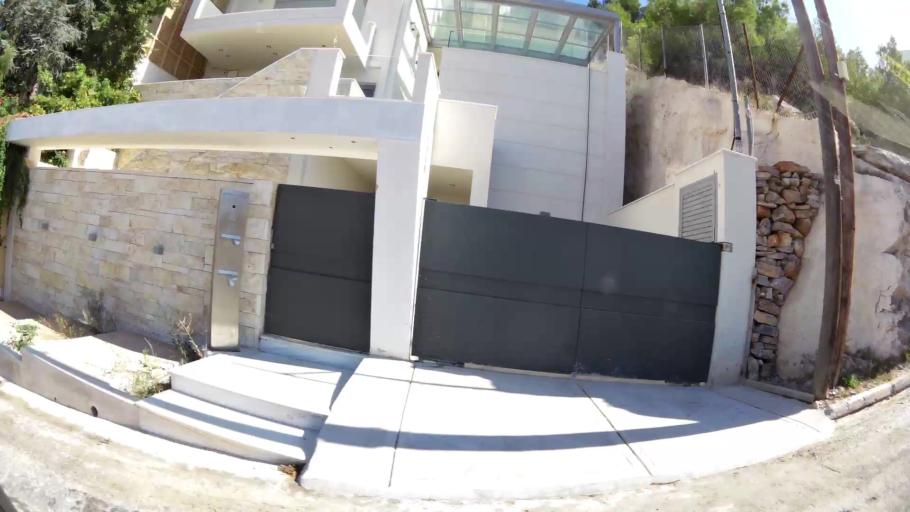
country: GR
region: Attica
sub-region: Nomarchia Anatolikis Attikis
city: Voula
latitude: 37.8591
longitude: 23.7827
